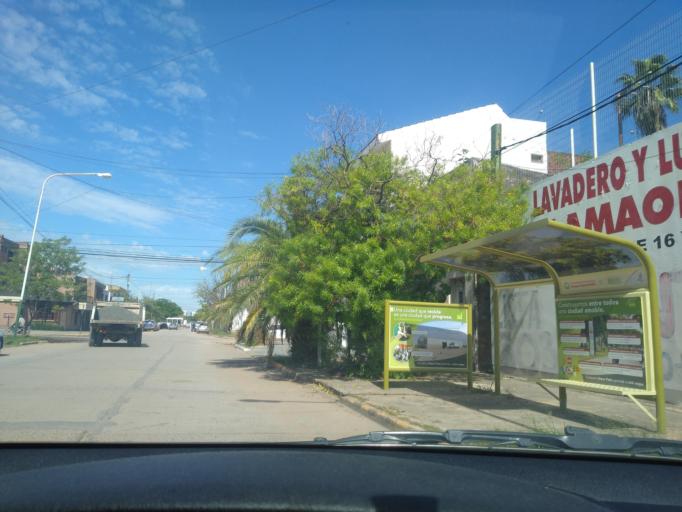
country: AR
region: Chaco
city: Presidencia Roque Saenz Pena
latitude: -26.7824
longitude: -60.4396
